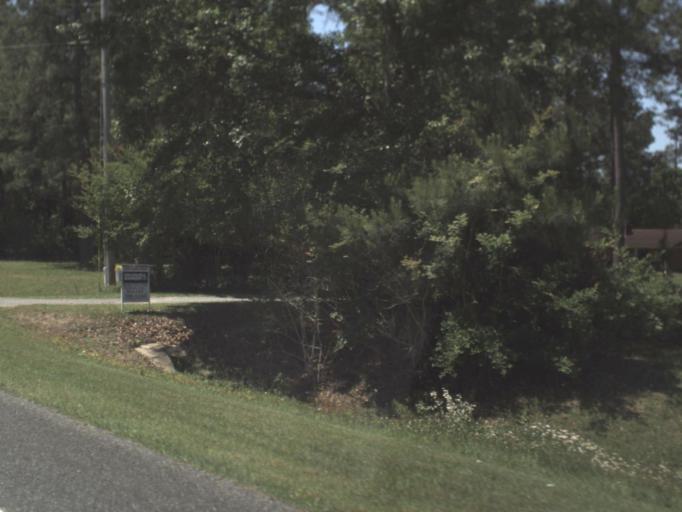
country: US
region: Florida
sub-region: Jefferson County
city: Monticello
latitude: 30.6143
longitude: -83.8724
